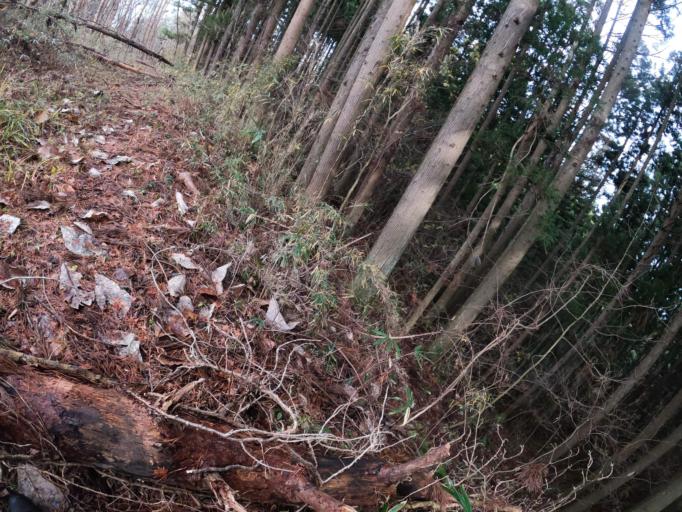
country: JP
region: Iwate
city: Ichinoseki
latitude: 38.8814
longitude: 141.1299
